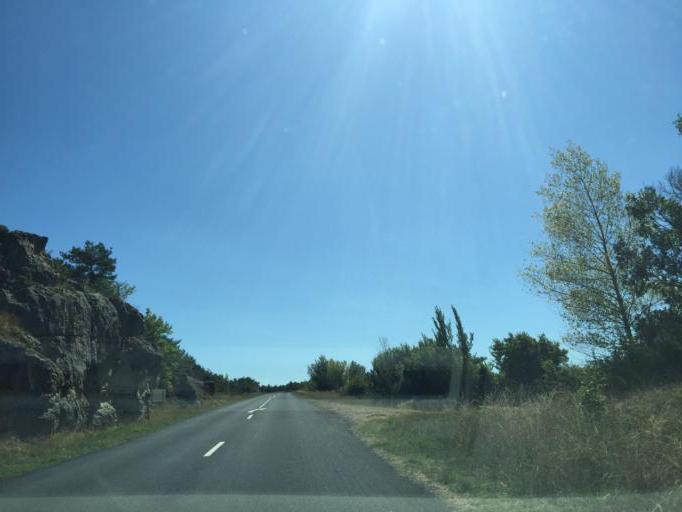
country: FR
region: Midi-Pyrenees
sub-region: Departement de l'Aveyron
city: La Cavalerie
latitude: 43.9067
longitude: 3.3106
